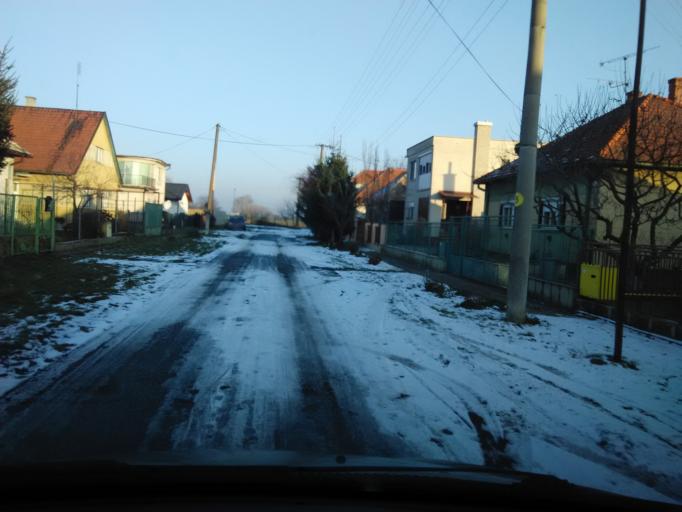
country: SK
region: Nitriansky
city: Tlmace
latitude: 48.2716
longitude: 18.5134
